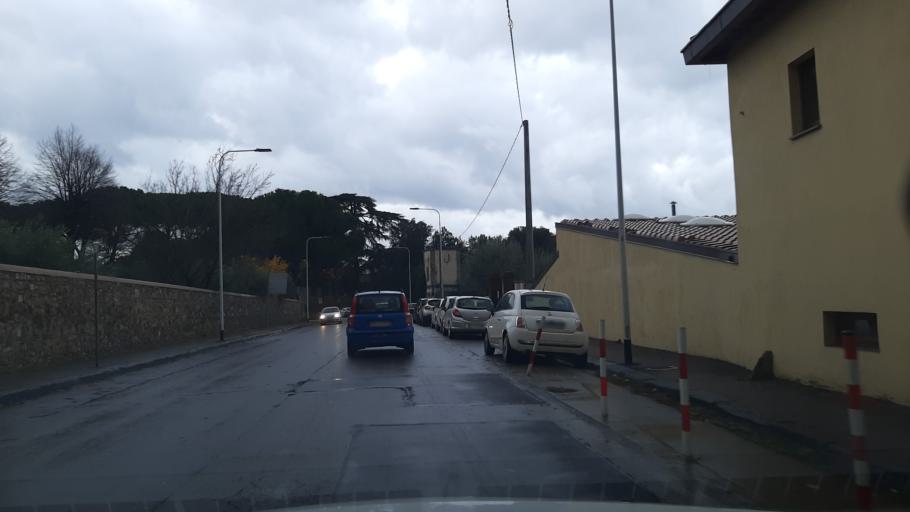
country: IT
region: Tuscany
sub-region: Province of Florence
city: Florence
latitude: 43.8113
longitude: 11.2500
